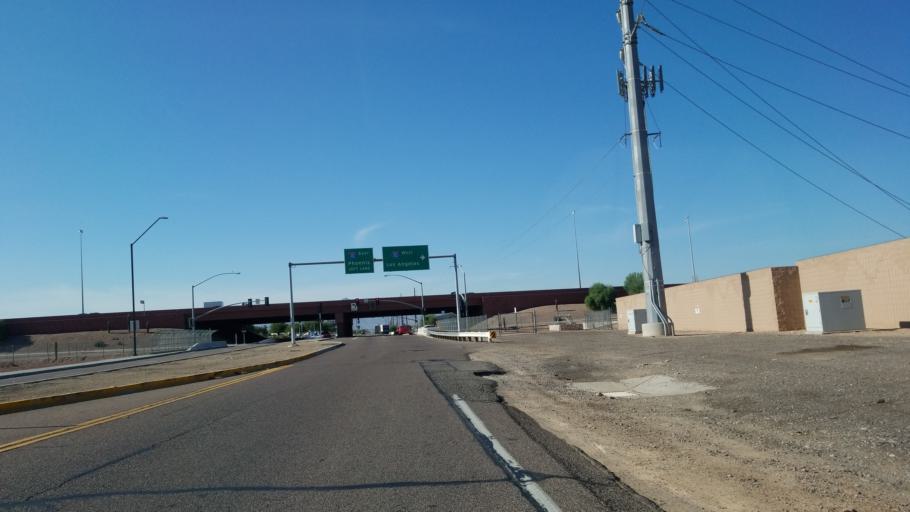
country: US
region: Arizona
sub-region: Maricopa County
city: Tolleson
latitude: 33.4629
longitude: -112.2900
